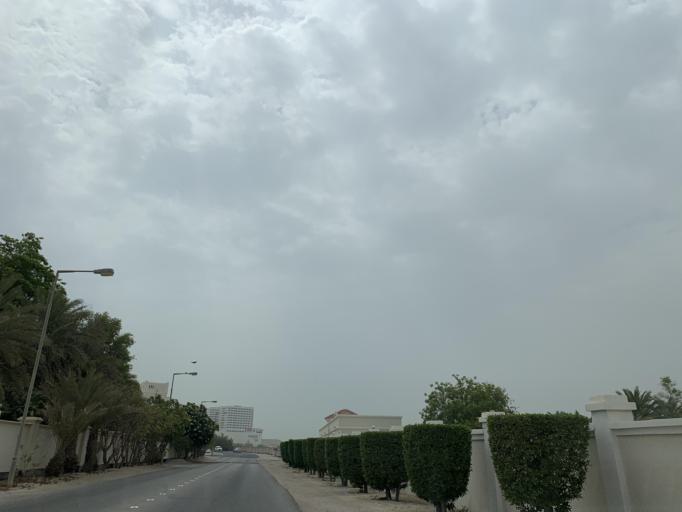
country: BH
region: Central Governorate
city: Madinat Hamad
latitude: 26.1790
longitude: 50.4753
